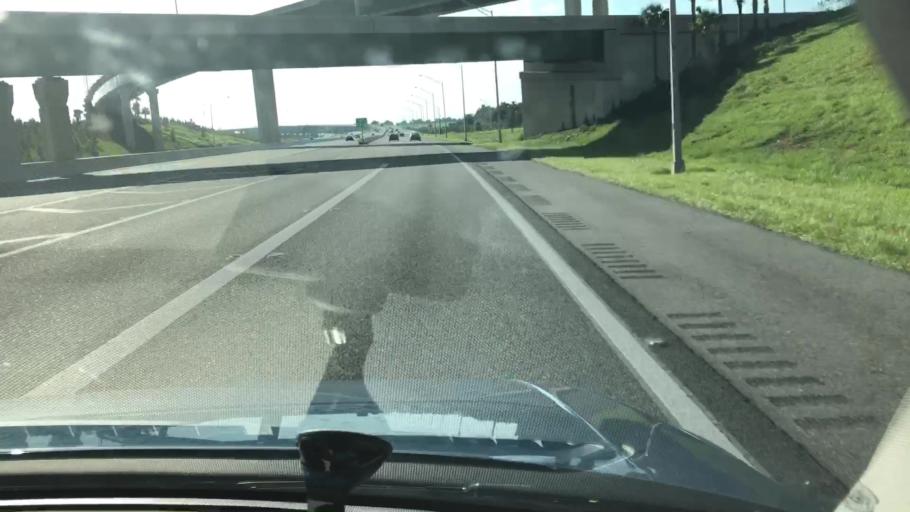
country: US
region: Florida
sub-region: Orange County
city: South Apopka
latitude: 28.6531
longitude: -81.5297
